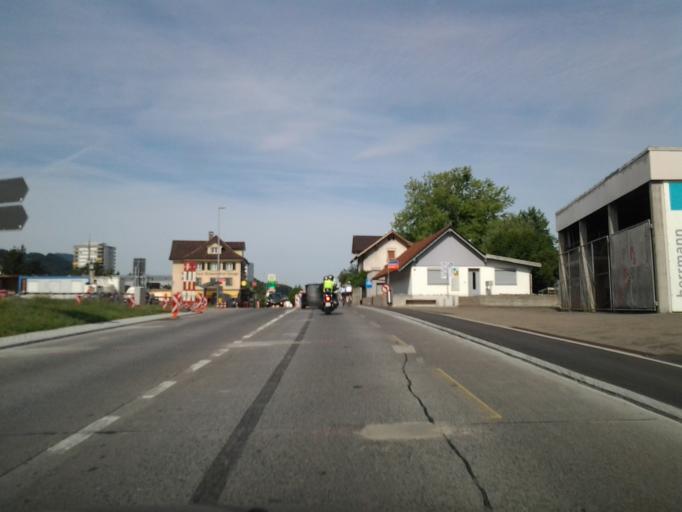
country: CH
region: Schwyz
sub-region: Bezirk Hoefe
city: Freienbach
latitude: 47.2021
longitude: 8.7921
